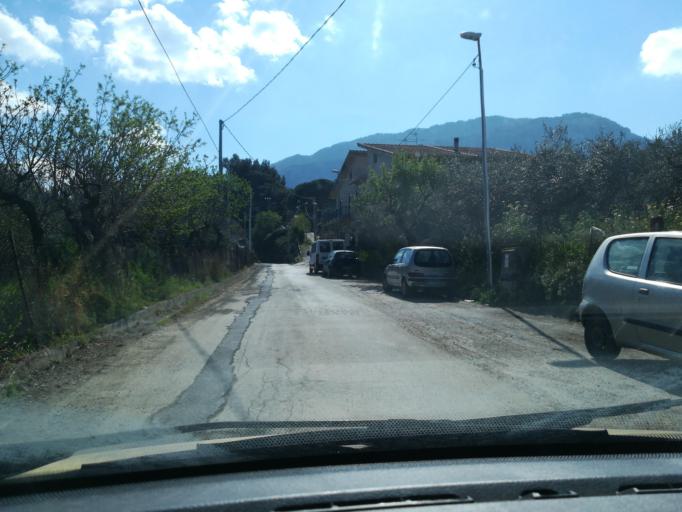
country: IT
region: Sicily
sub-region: Palermo
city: Cannizzaro-Favara
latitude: 38.0452
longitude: 13.2701
